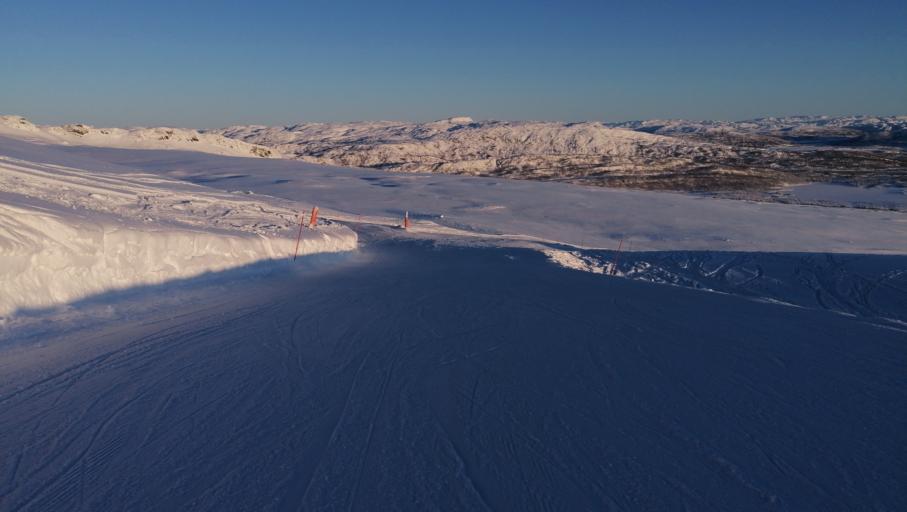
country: NO
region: Aust-Agder
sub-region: Bykle
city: Hovden
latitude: 59.5811
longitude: 7.3318
